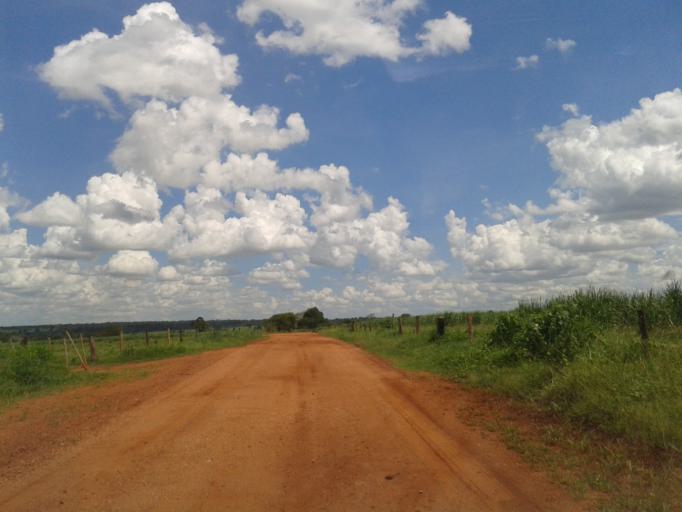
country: BR
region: Minas Gerais
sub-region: Santa Vitoria
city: Santa Vitoria
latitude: -19.1600
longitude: -50.5992
